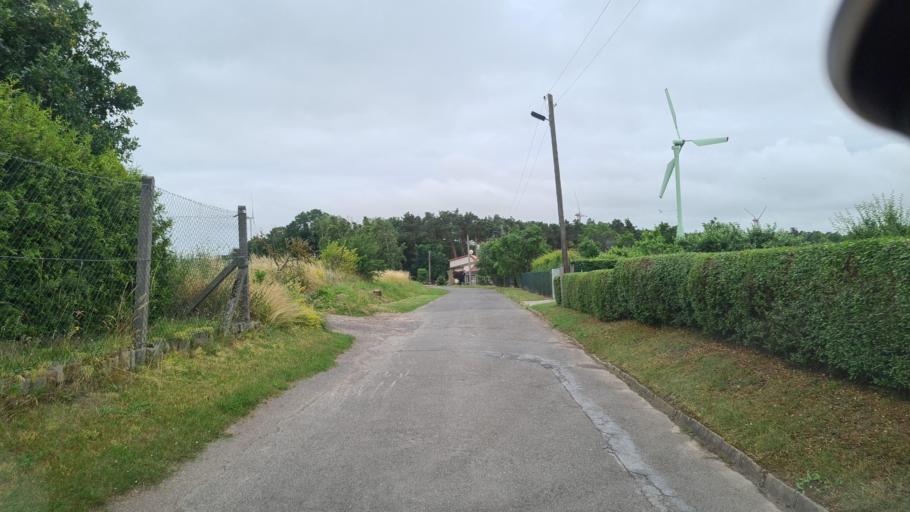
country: DE
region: Brandenburg
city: Juterbog
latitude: 51.9705
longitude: 13.1695
